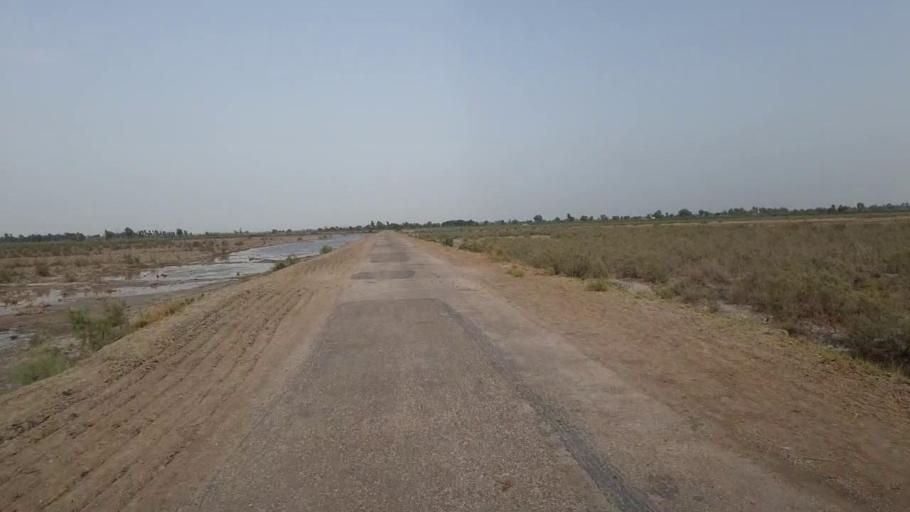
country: PK
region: Sindh
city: Daulatpur
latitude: 26.5462
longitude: 68.0827
